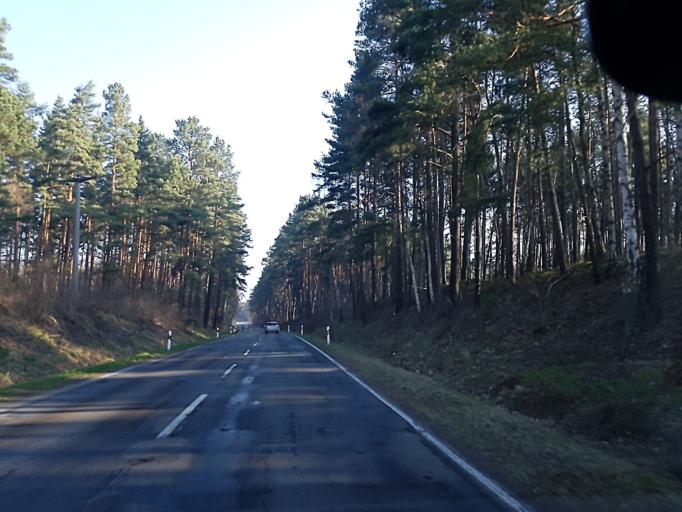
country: DE
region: Brandenburg
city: Bronkow
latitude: 51.7061
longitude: 13.9200
